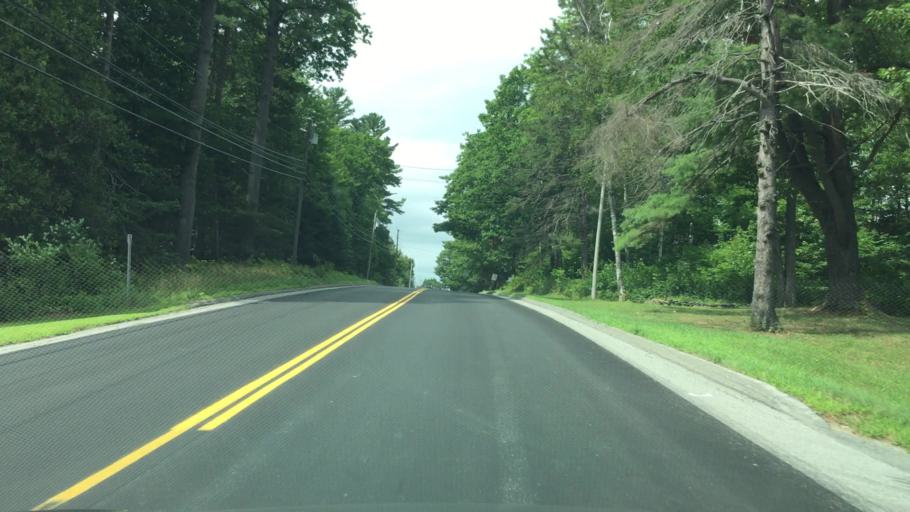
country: US
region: Maine
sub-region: Hancock County
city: Bucksport
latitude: 44.6041
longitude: -68.8172
